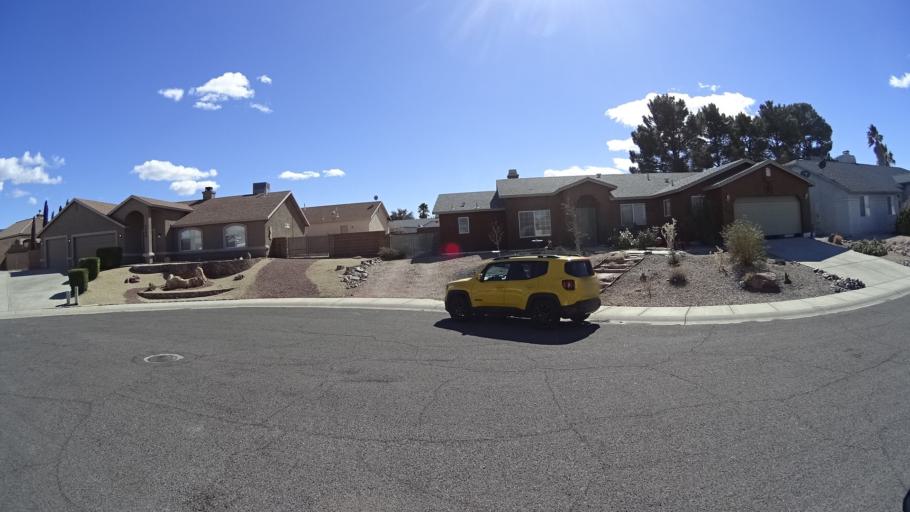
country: US
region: Arizona
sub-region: Mohave County
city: Kingman
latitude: 35.1915
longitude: -114.0077
